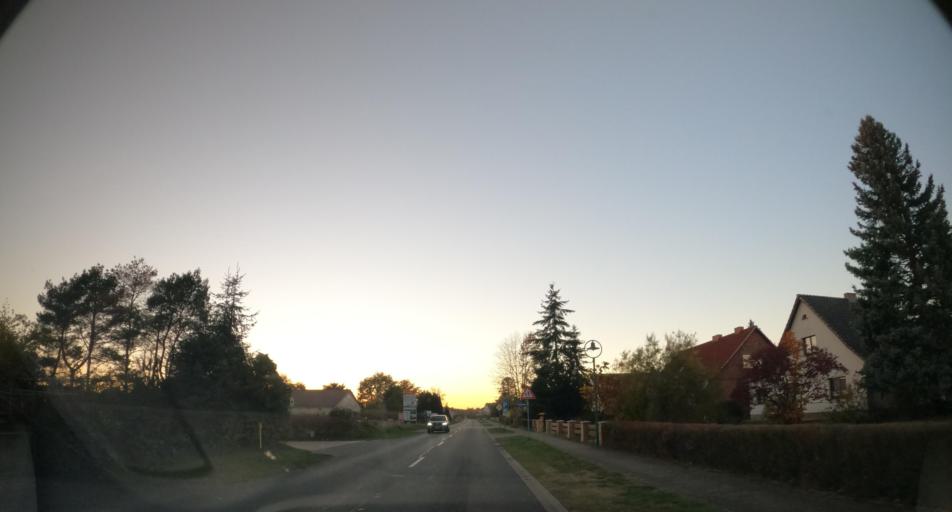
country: DE
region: Mecklenburg-Vorpommern
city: Ueckermunde
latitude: 53.7670
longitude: 13.9688
